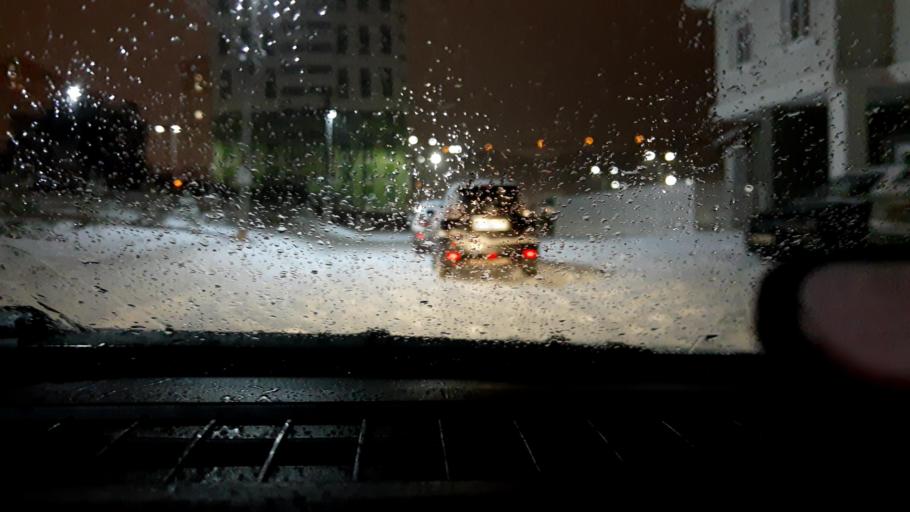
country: RU
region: Nizjnij Novgorod
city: Afonino
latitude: 56.2776
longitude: 44.0918
